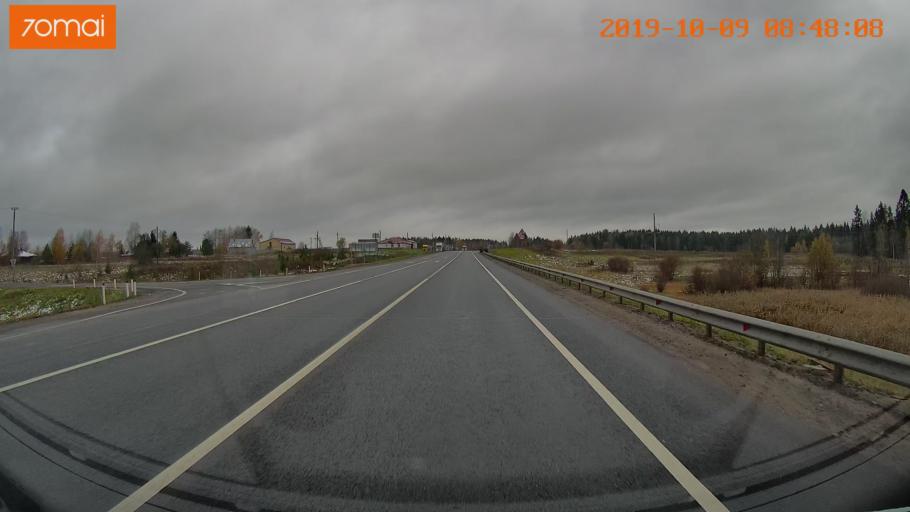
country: RU
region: Vologda
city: Vologda
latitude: 59.0711
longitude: 40.0309
